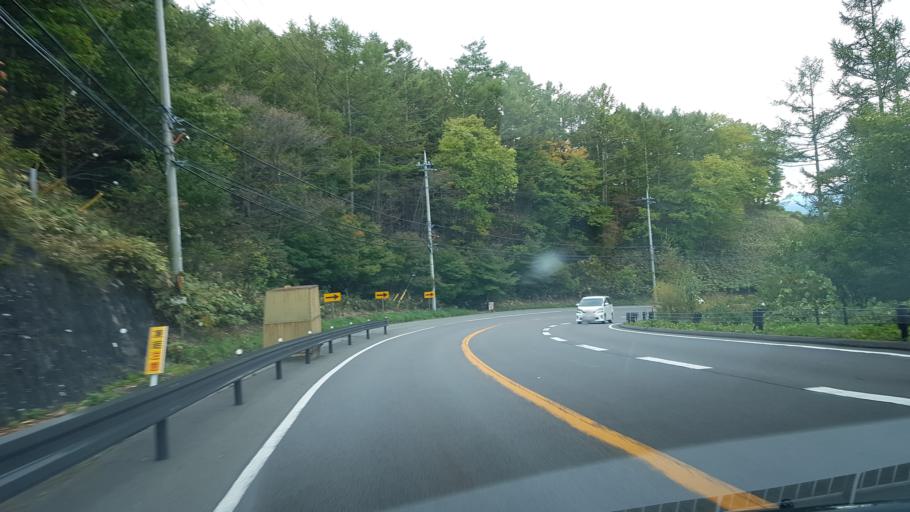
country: JP
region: Gunma
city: Nakanojomachi
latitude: 36.6005
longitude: 138.5869
